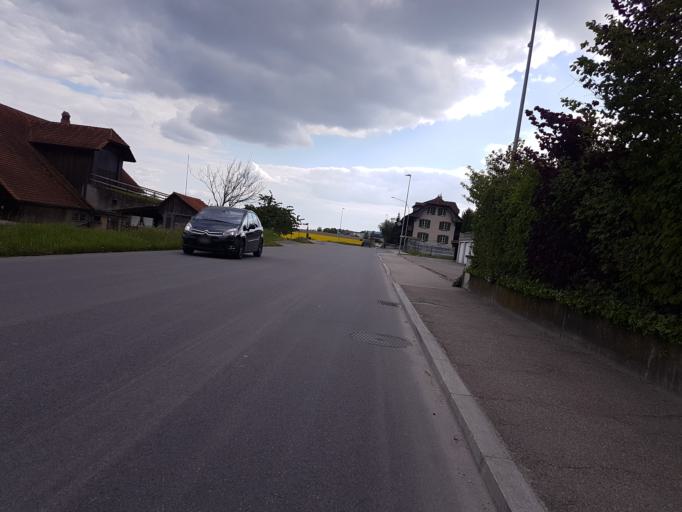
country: CH
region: Bern
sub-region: Biel/Bienne District
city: Orpund
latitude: 47.1469
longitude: 7.3191
